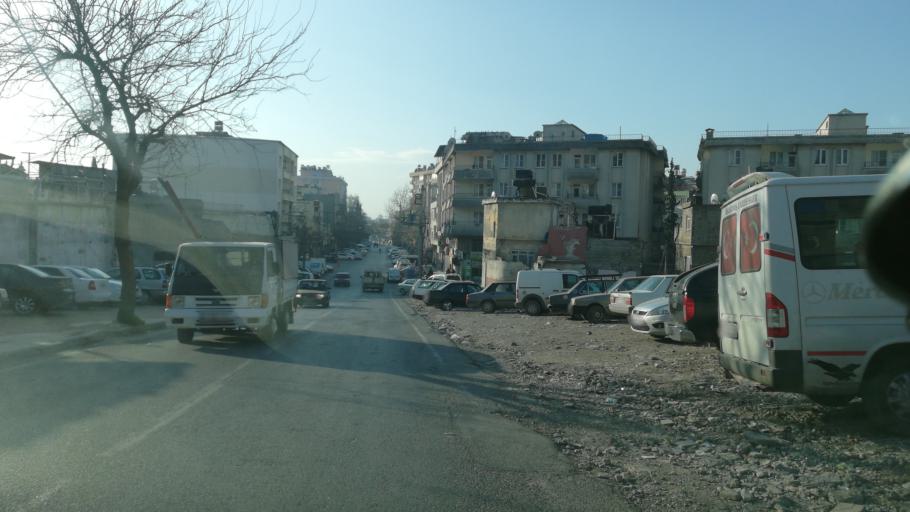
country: TR
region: Kahramanmaras
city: Kahramanmaras
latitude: 37.5814
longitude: 36.9315
